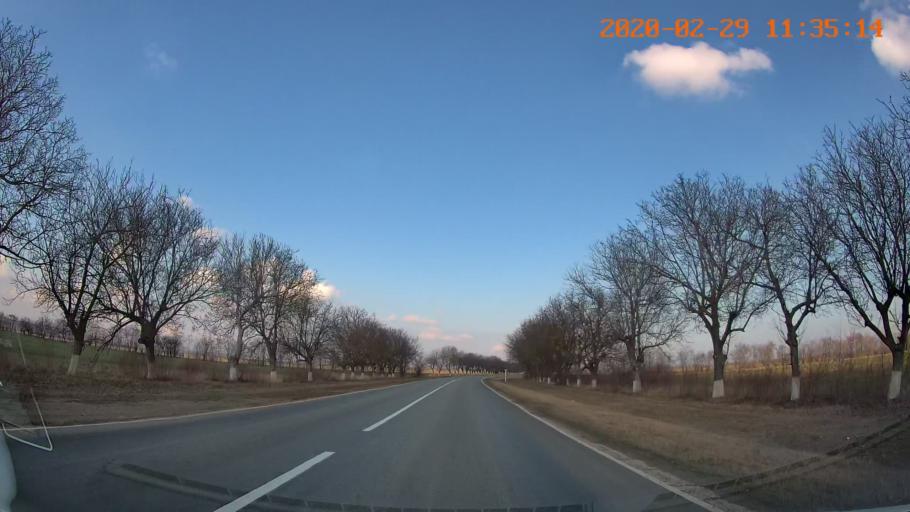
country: MD
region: Rezina
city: Saharna
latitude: 47.5773
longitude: 29.0651
